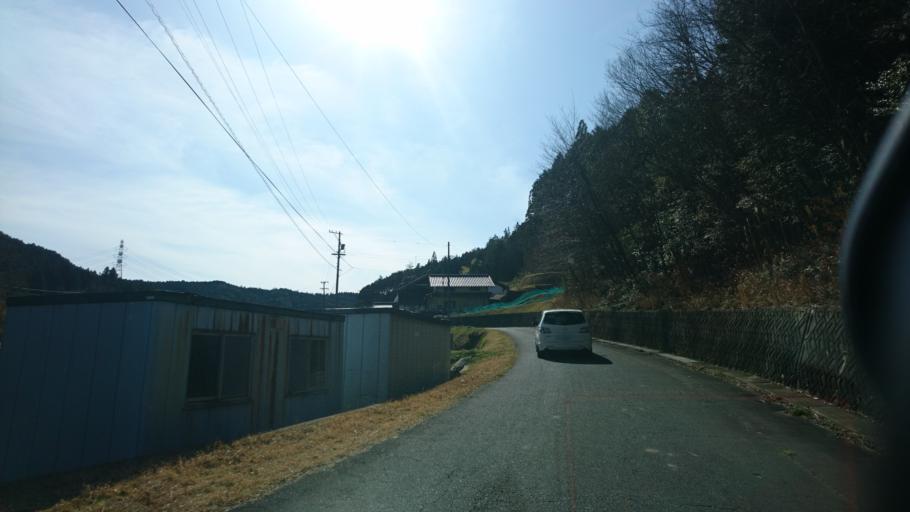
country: JP
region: Gifu
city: Mizunami
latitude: 35.4632
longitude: 137.3496
